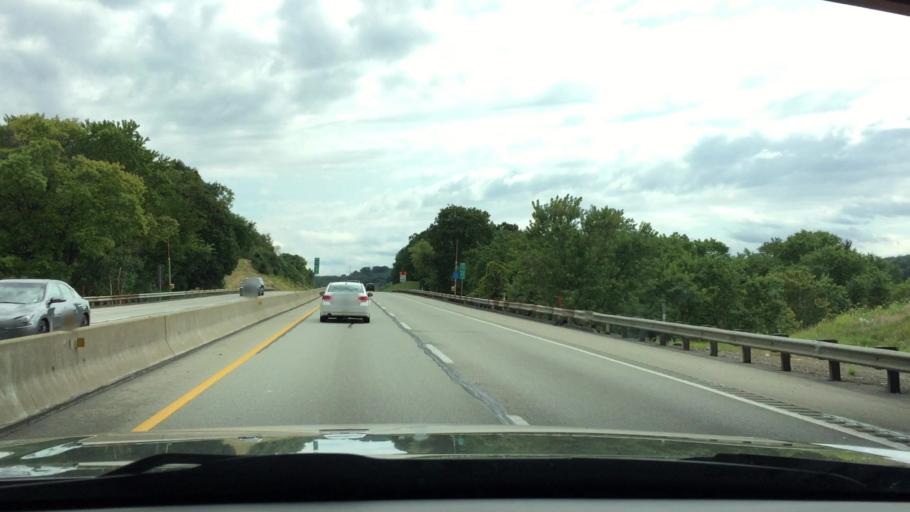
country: US
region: Pennsylvania
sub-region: Allegheny County
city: Bradford Woods
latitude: 40.6608
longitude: -80.0906
